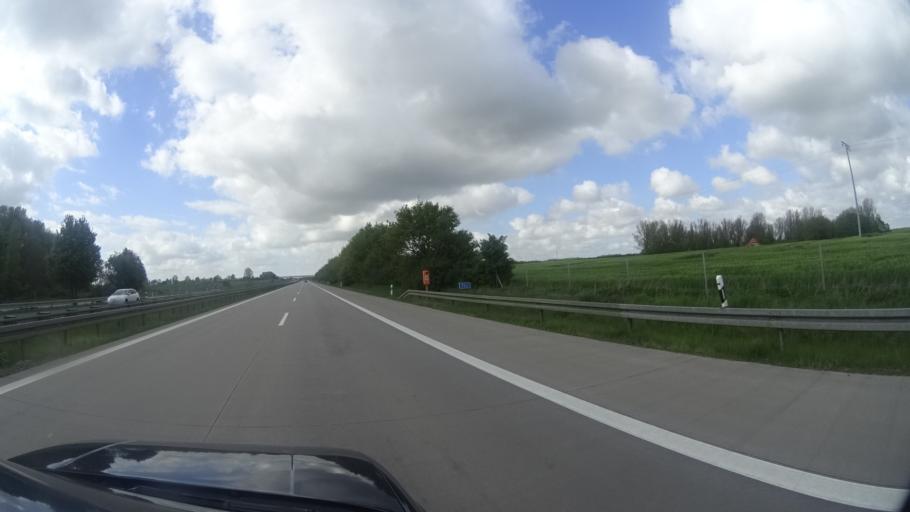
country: DE
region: Mecklenburg-Vorpommern
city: Laage
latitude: 53.9033
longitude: 12.2475
